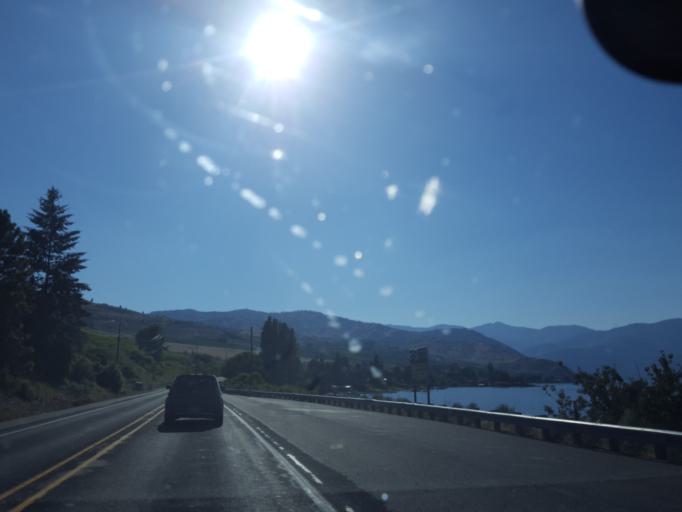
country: US
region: Washington
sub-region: Chelan County
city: Chelan
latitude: 47.8359
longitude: -120.0689
